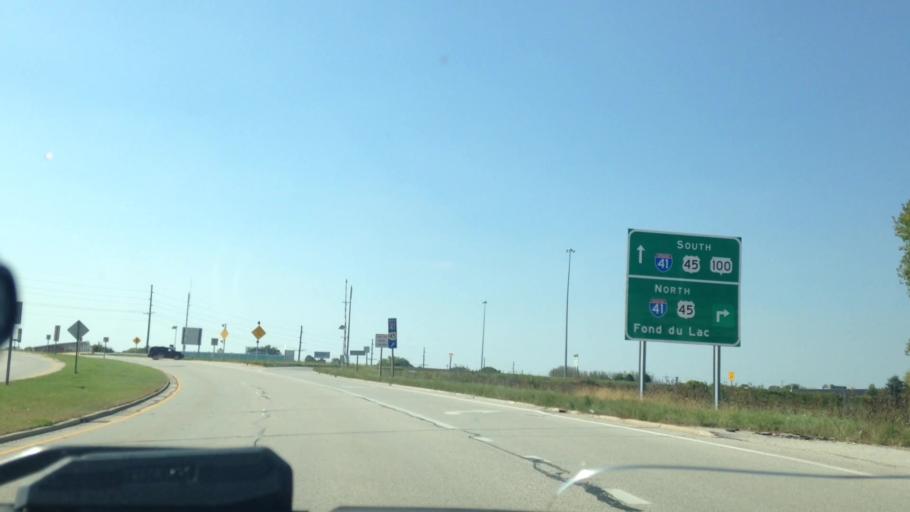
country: US
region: Wisconsin
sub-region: Waukesha County
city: Menomonee Falls
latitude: 43.1783
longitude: -88.0879
